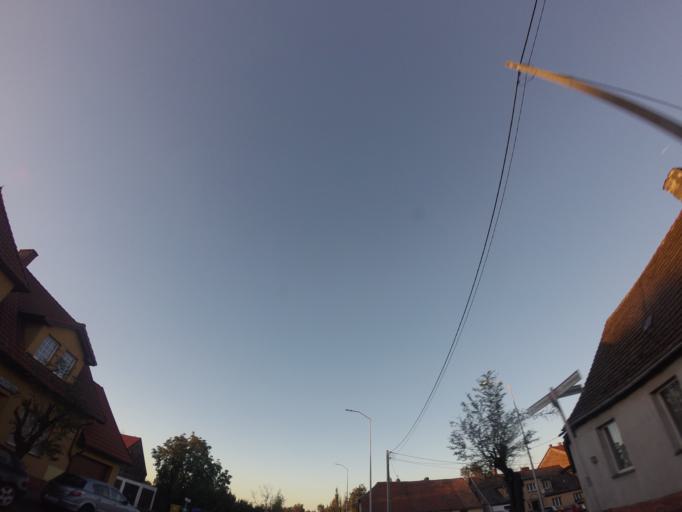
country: PL
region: Lubusz
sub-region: Powiat strzelecko-drezdenecki
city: Drezdenko
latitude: 52.8403
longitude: 15.8353
